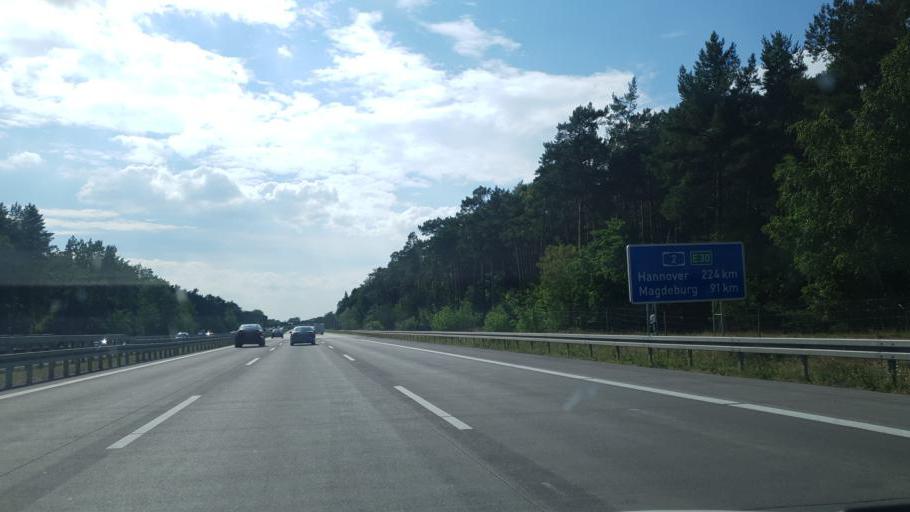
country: DE
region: Brandenburg
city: Gross Kreutz
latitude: 52.3404
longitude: 12.7438
